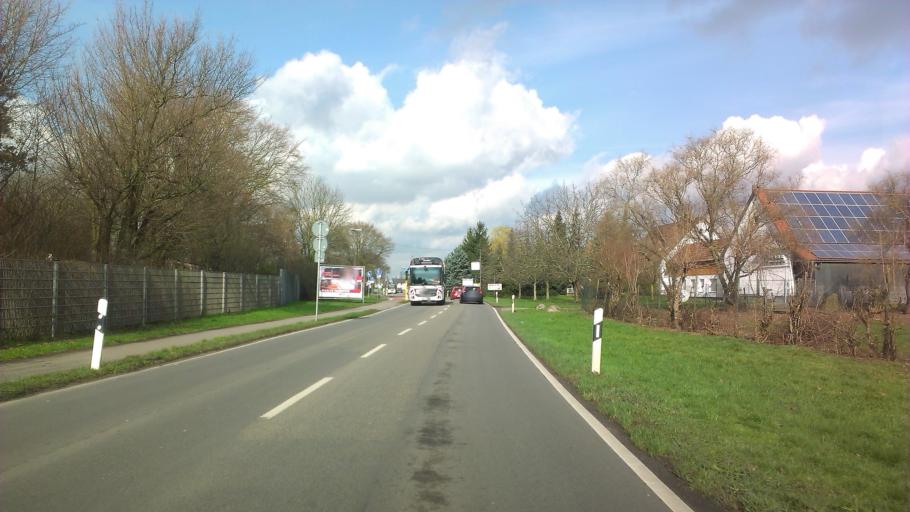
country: DE
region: Baden-Wuerttemberg
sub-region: Karlsruhe Region
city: Eppelheim
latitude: 49.3984
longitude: 8.6547
